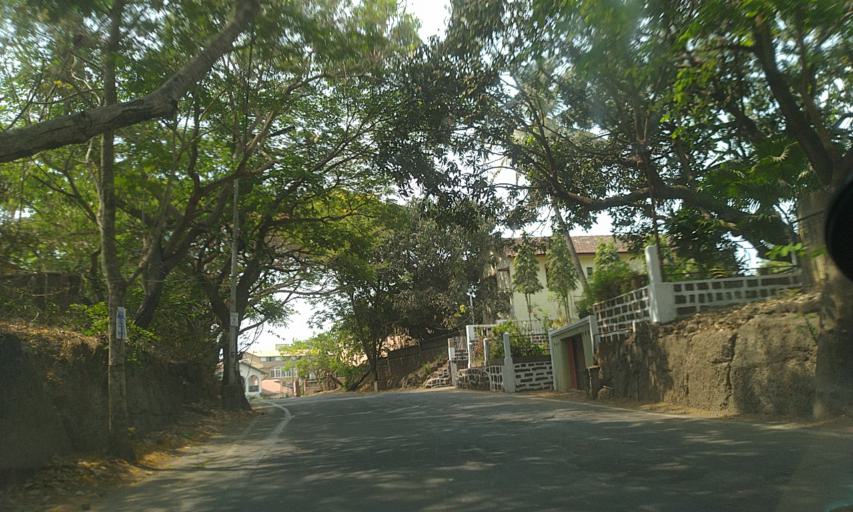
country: IN
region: Goa
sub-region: North Goa
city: Panaji
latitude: 15.4920
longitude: 73.8238
